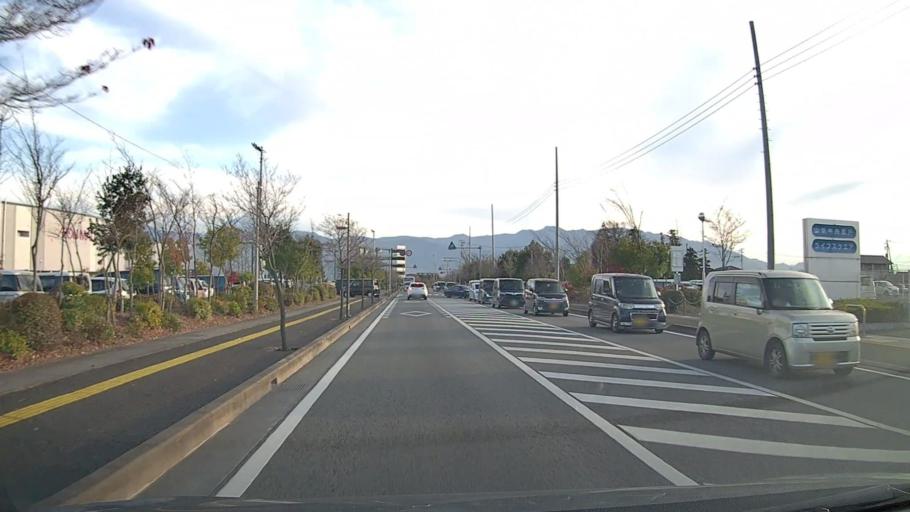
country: JP
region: Yamanashi
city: Ryuo
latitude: 35.6237
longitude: 138.5253
